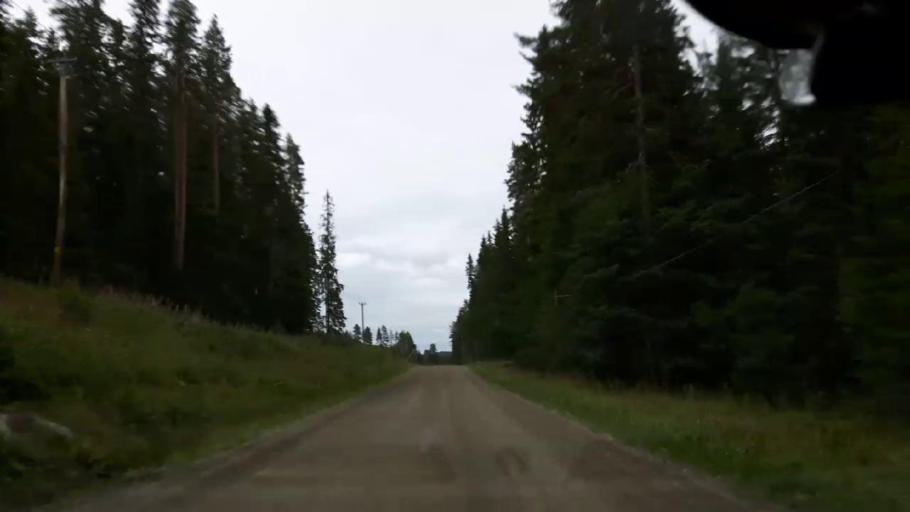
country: SE
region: Jaemtland
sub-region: Braecke Kommun
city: Braecke
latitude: 63.0443
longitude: 15.3544
